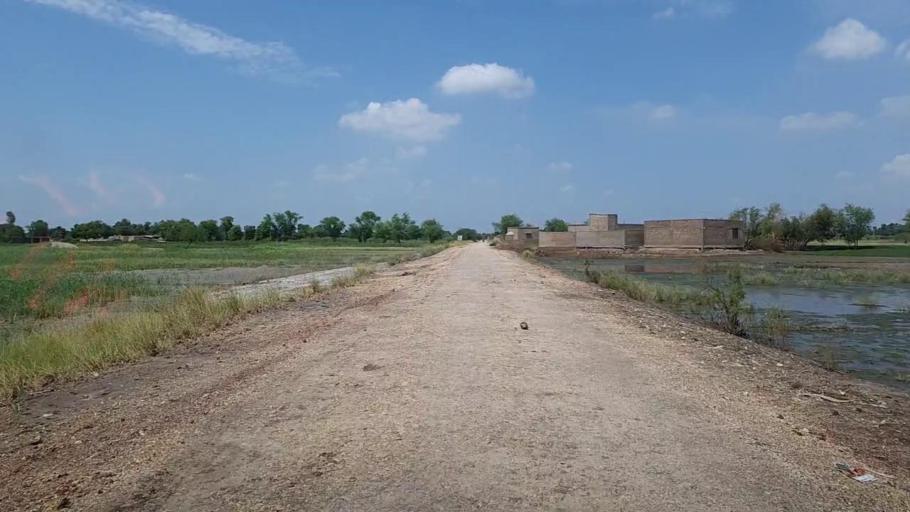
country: PK
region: Sindh
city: Bhiria
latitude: 26.9735
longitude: 68.2402
